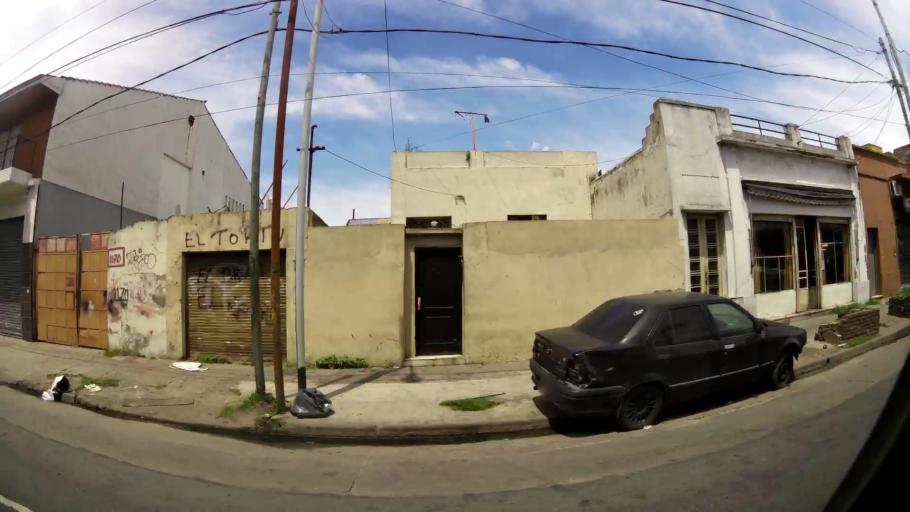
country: AR
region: Buenos Aires
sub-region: Partido de Avellaneda
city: Avellaneda
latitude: -34.6721
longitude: -58.3945
